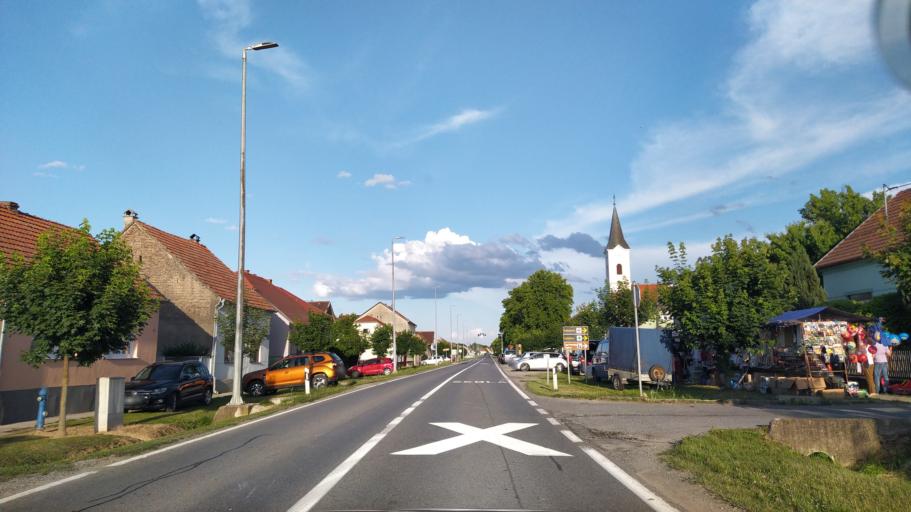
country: HR
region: Virovitick-Podravska
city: Cacinci
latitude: 45.6007
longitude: 17.8724
